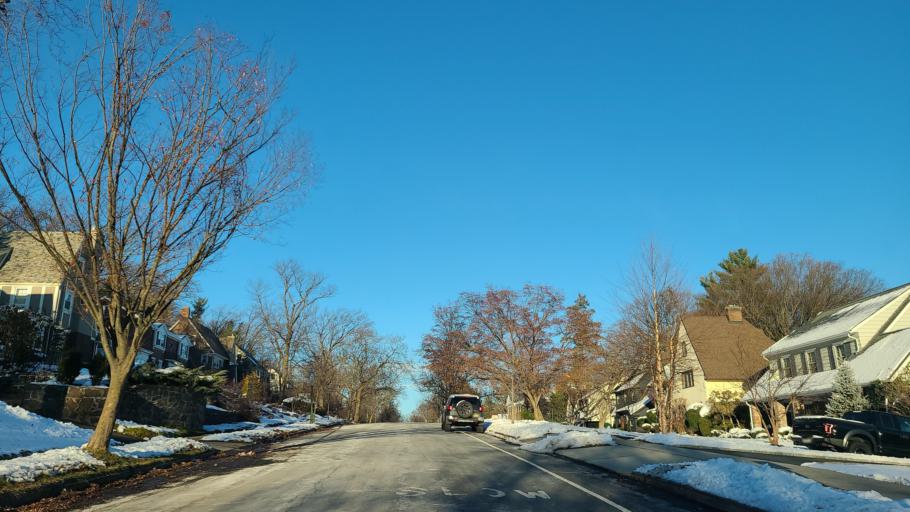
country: US
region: New Jersey
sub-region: Essex County
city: South Orange
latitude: 40.7478
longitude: -74.2741
